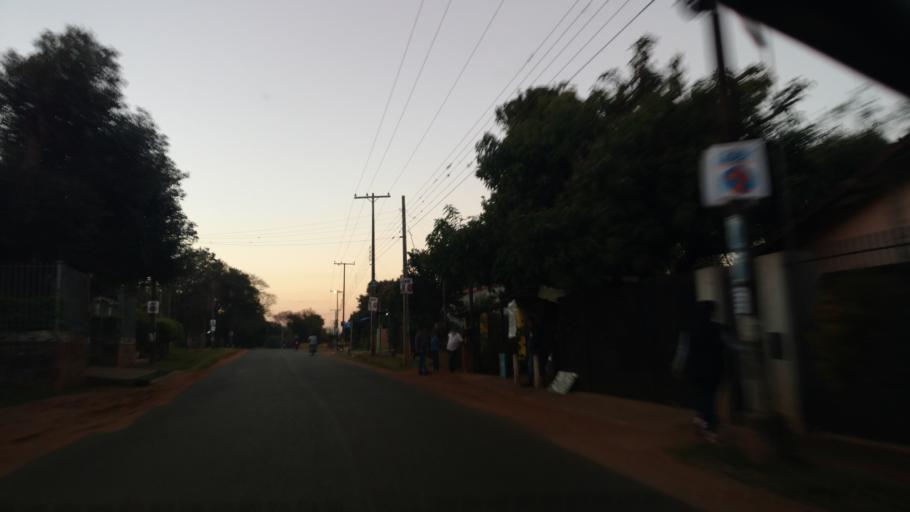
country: PY
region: Central
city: Guarambare
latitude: -25.4686
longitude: -57.4092
